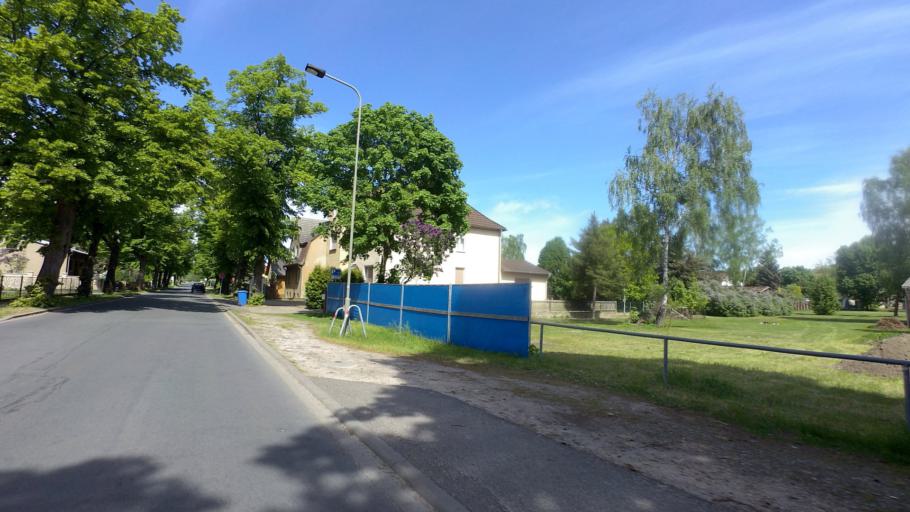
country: DE
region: Brandenburg
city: Sperenberg
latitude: 52.1446
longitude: 13.3649
